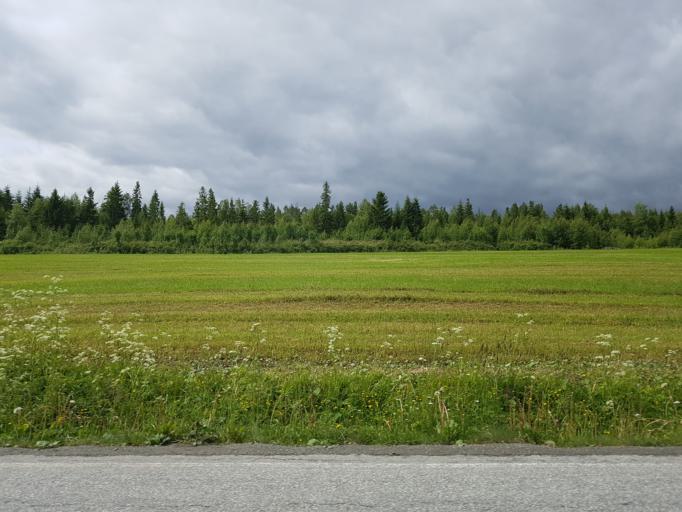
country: NO
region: Sor-Trondelag
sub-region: Selbu
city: Mebonden
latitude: 63.2622
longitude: 11.0814
